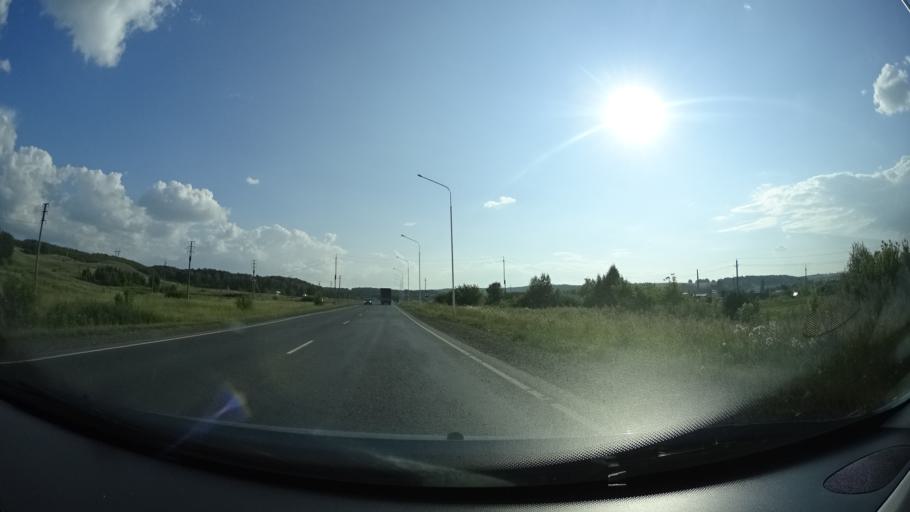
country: RU
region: Tatarstan
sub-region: Bavlinskiy Rayon
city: Bavly
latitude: 54.4633
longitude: 53.2899
